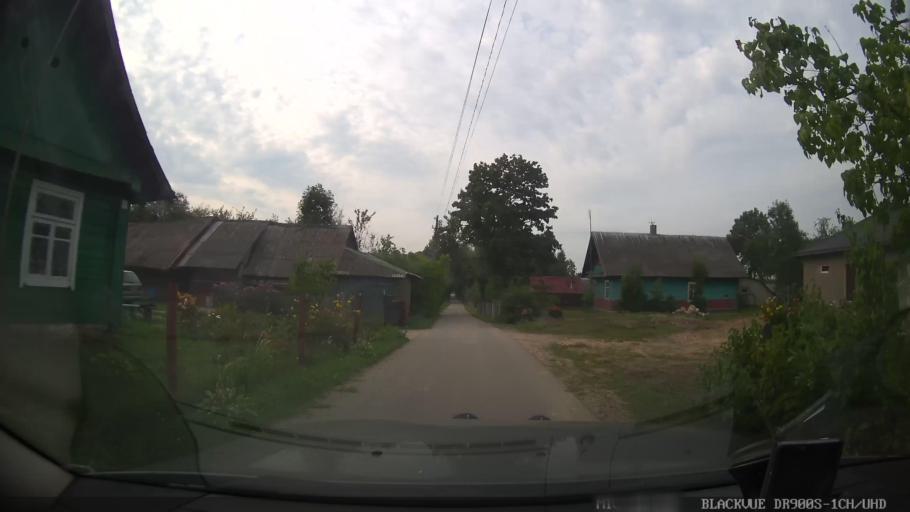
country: BY
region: Grodnenskaya
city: Ashmyany
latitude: 54.5318
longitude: 25.6675
